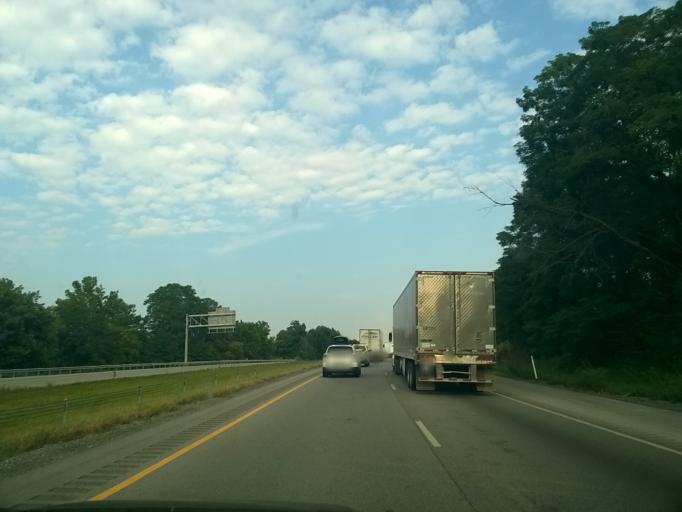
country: US
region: Indiana
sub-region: Putnam County
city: Cloverdale
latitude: 39.5331
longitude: -86.8499
